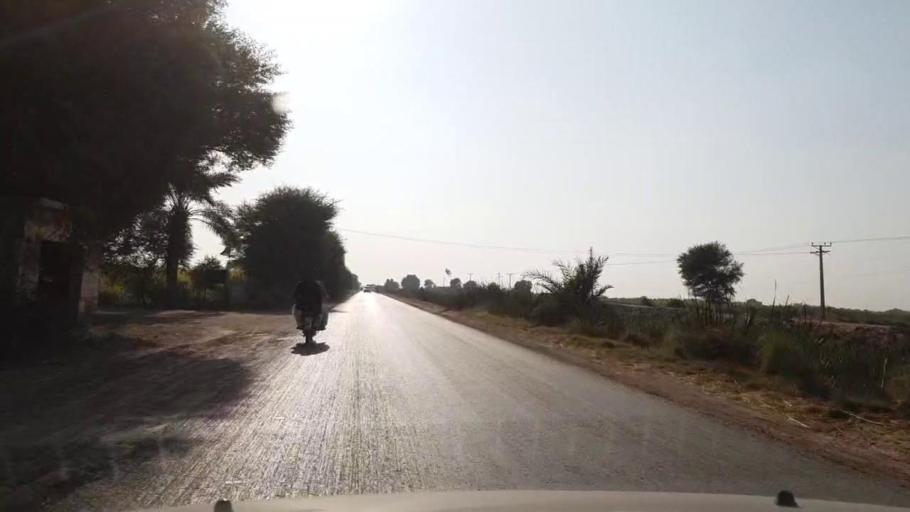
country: PK
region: Sindh
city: Tando Muhammad Khan
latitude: 25.0293
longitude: 68.4237
